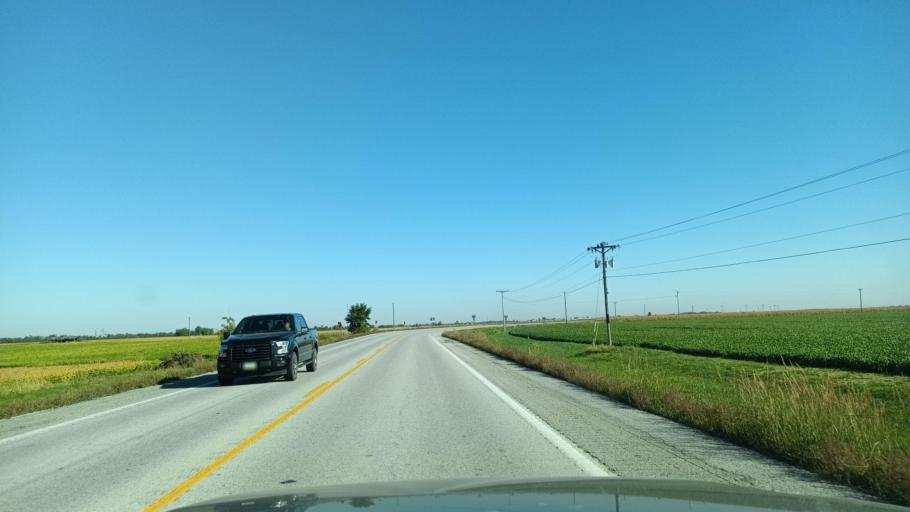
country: US
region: Missouri
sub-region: Audrain County
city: Vandalia
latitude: 39.4086
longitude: -91.6415
